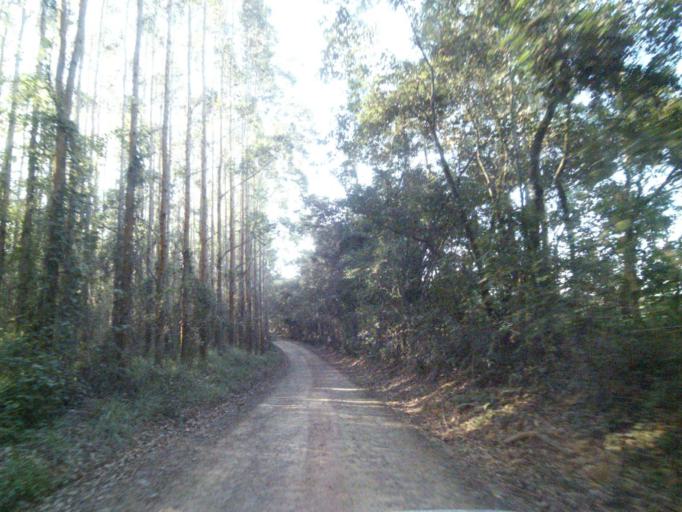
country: BR
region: Parana
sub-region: Telemaco Borba
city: Telemaco Borba
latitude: -24.5016
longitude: -50.5980
